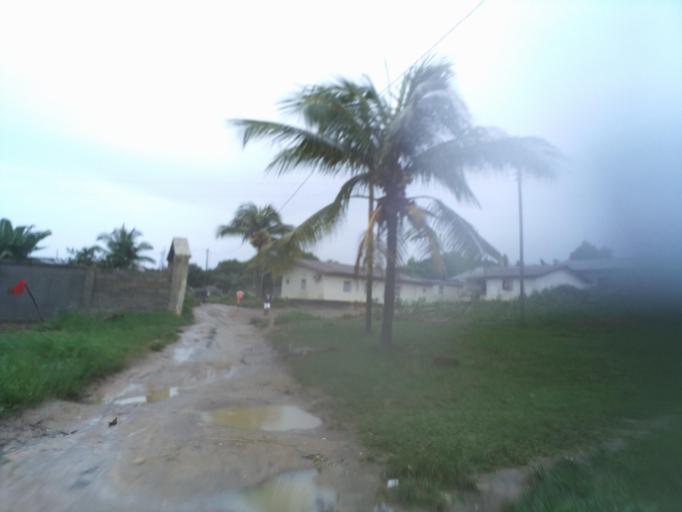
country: SL
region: Eastern Province
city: Kenema
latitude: 7.8550
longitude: -11.1919
